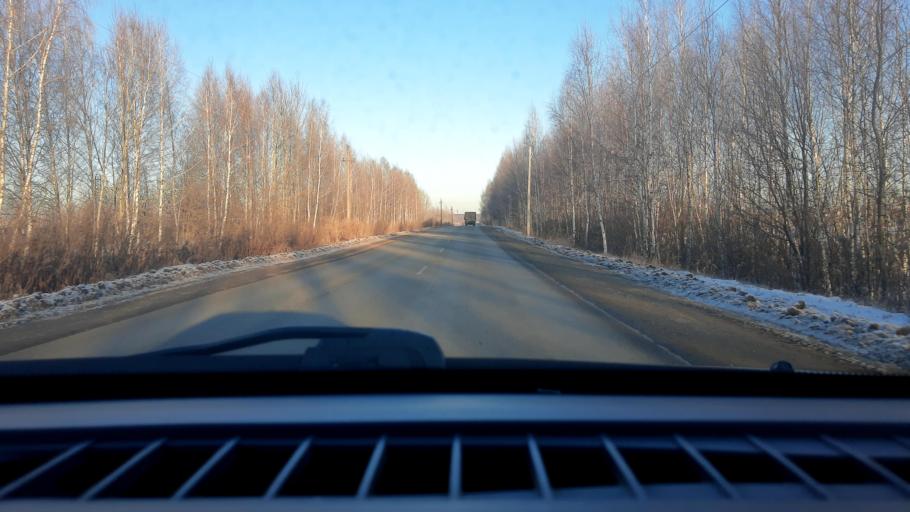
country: RU
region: Nizjnij Novgorod
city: Bor
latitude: 56.3869
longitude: 44.0792
